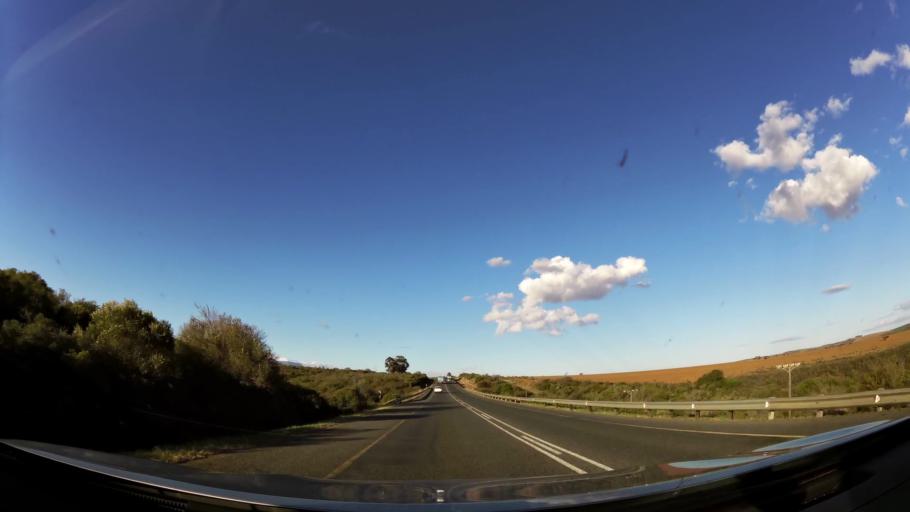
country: ZA
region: Western Cape
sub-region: Eden District Municipality
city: Riversdale
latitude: -34.0854
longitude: 20.9906
